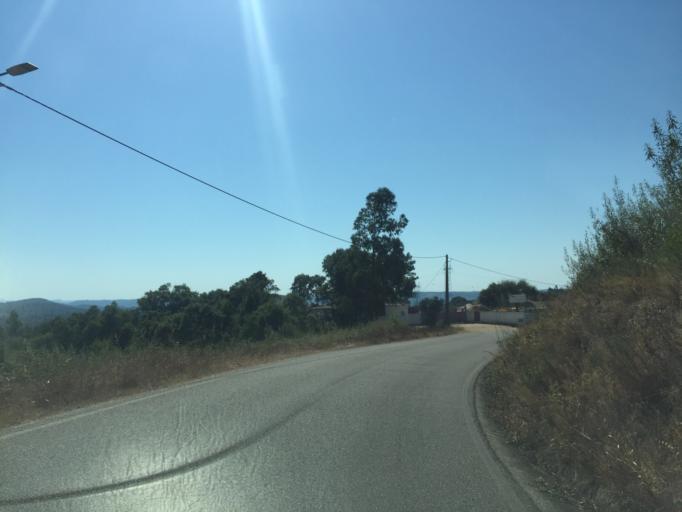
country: PT
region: Santarem
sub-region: Tomar
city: Tomar
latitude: 39.5803
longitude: -8.3262
